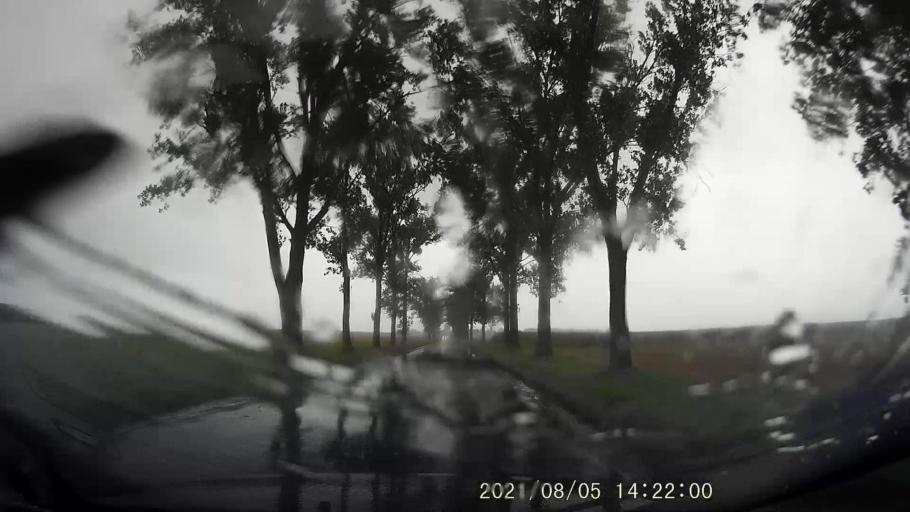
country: PL
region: Opole Voivodeship
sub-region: Powiat nyski
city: Korfantow
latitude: 50.4737
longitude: 17.6633
